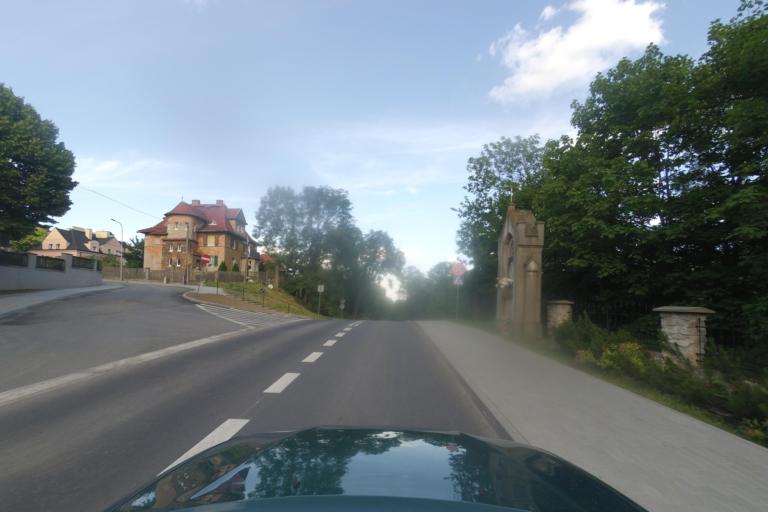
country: PL
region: Lower Silesian Voivodeship
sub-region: Powiat zabkowicki
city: Bardo
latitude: 50.5069
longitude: 16.7465
